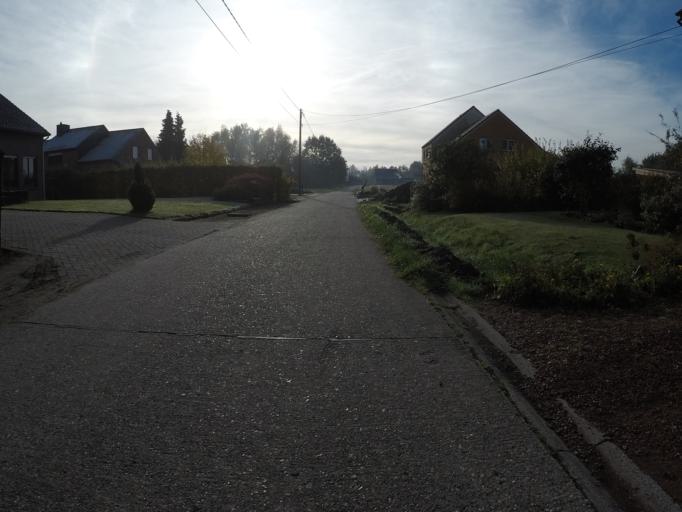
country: BE
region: Flanders
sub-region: Provincie Vlaams-Brabant
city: Begijnendijk
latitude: 50.9987
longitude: 4.7732
